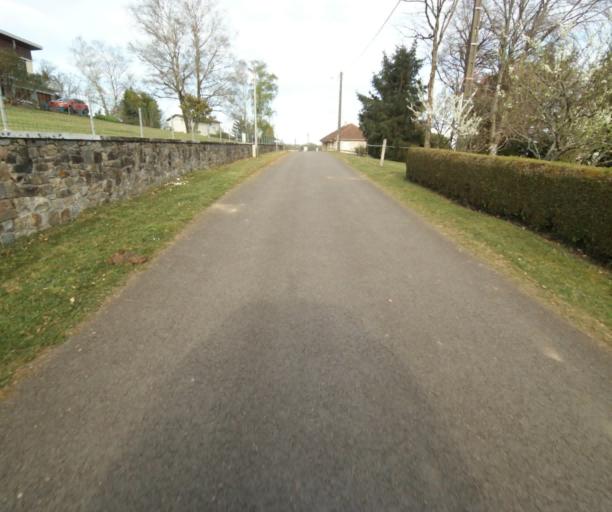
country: FR
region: Limousin
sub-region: Departement de la Correze
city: Naves
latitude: 45.3188
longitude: 1.7636
